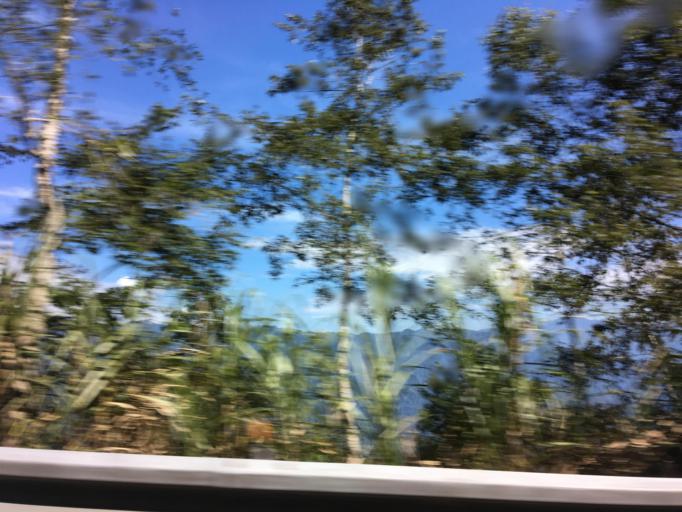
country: TW
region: Taiwan
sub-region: Yilan
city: Yilan
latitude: 24.5349
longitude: 121.5174
